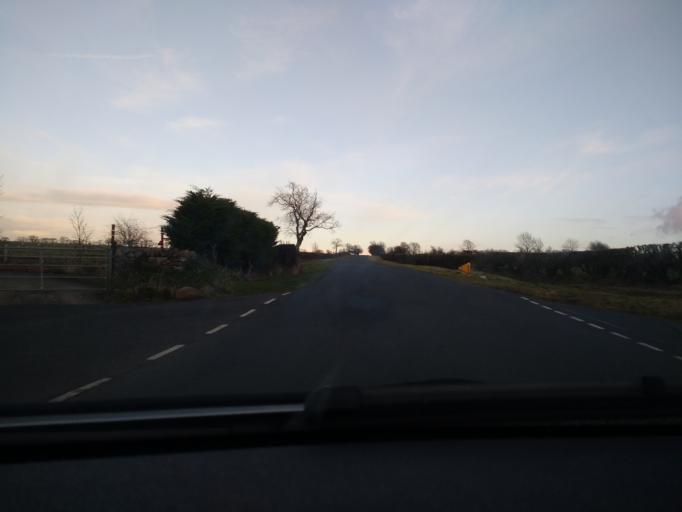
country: GB
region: England
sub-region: Cumbria
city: Carlisle
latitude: 54.7306
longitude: -2.9708
